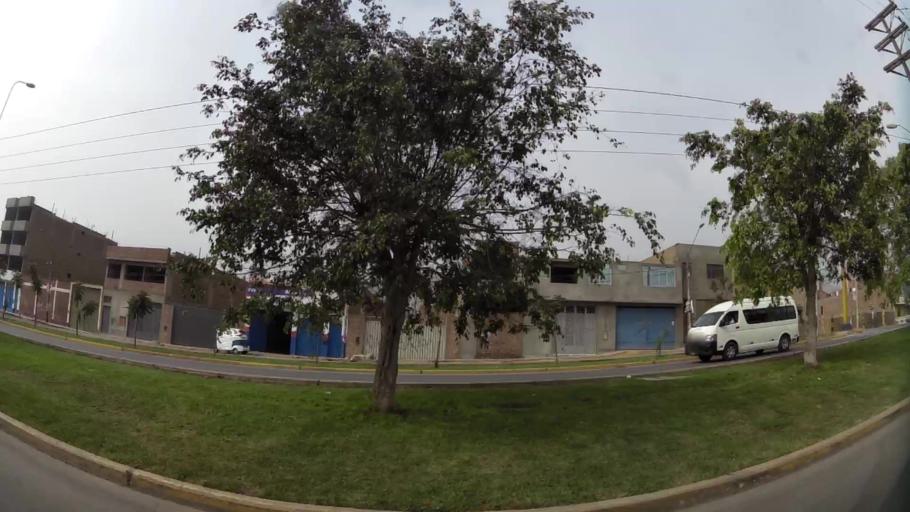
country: PE
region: Lima
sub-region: Lima
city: Santa Maria
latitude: -11.9987
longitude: -76.8340
